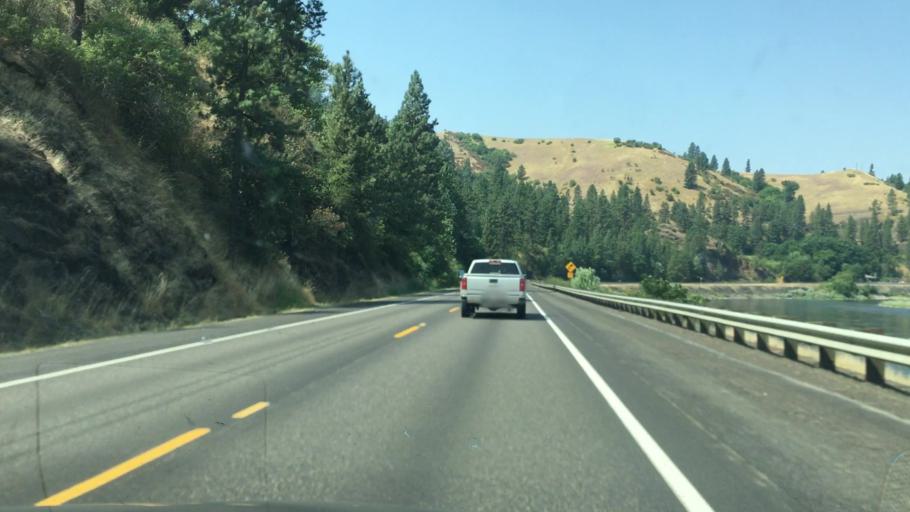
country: US
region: Idaho
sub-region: Nez Perce County
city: Lapwai
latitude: 46.5057
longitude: -116.5433
